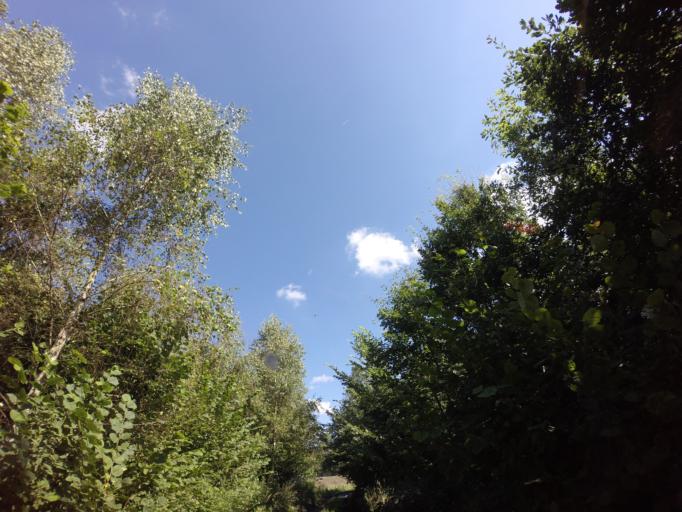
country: PL
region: West Pomeranian Voivodeship
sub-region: Powiat choszczenski
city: Drawno
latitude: 53.2319
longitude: 15.6522
